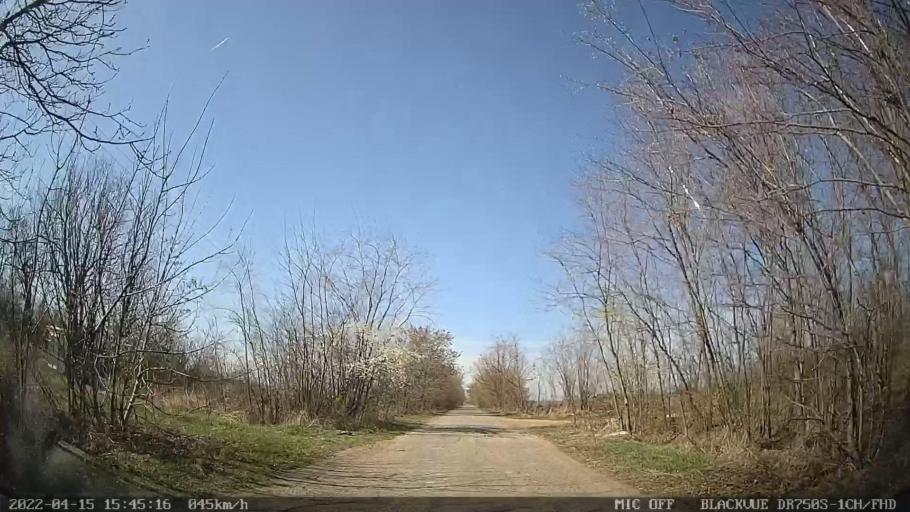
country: MD
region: Raionul Ocnita
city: Otaci
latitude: 48.3755
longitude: 27.9189
